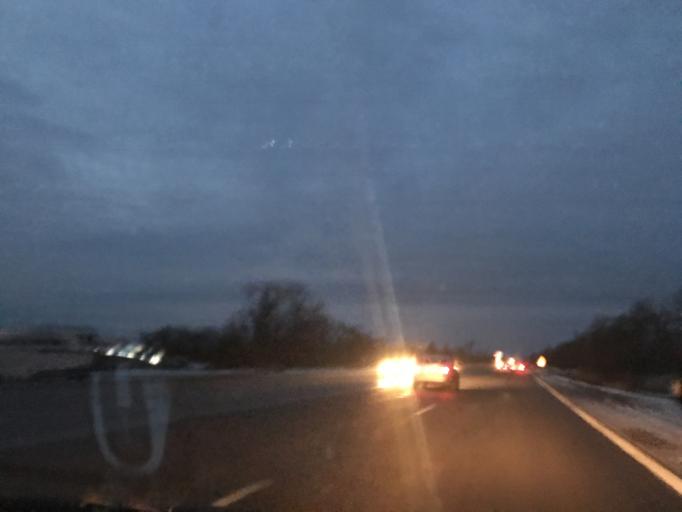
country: RU
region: Rostov
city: Bataysk
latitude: 47.0338
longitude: 39.7404
